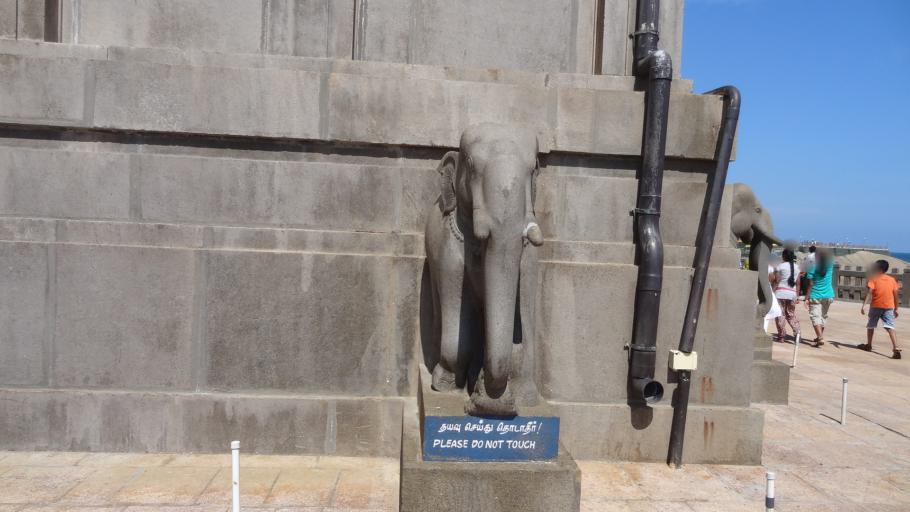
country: IN
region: Tamil Nadu
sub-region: Kanniyakumari
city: Kanniyakumari
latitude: 8.0777
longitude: 77.5539
